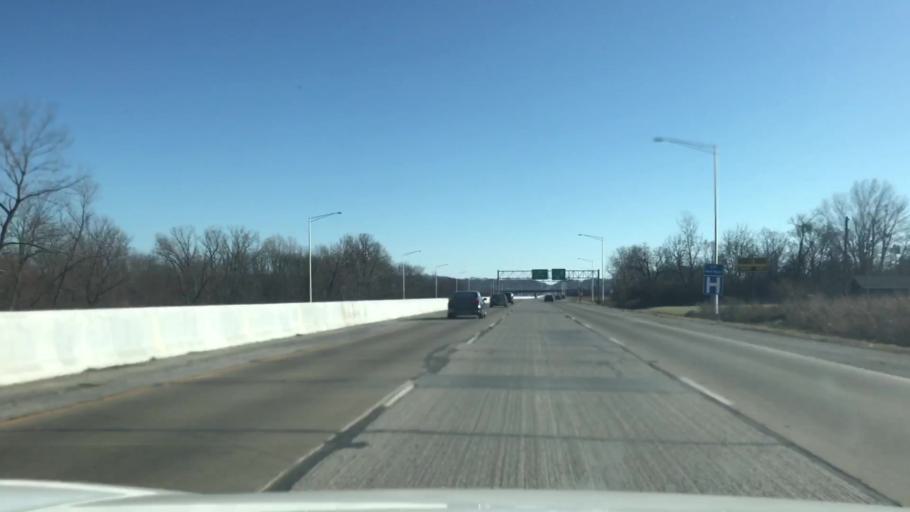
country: US
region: Illinois
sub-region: Saint Clair County
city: Alorton
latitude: 38.5884
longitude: -90.1146
